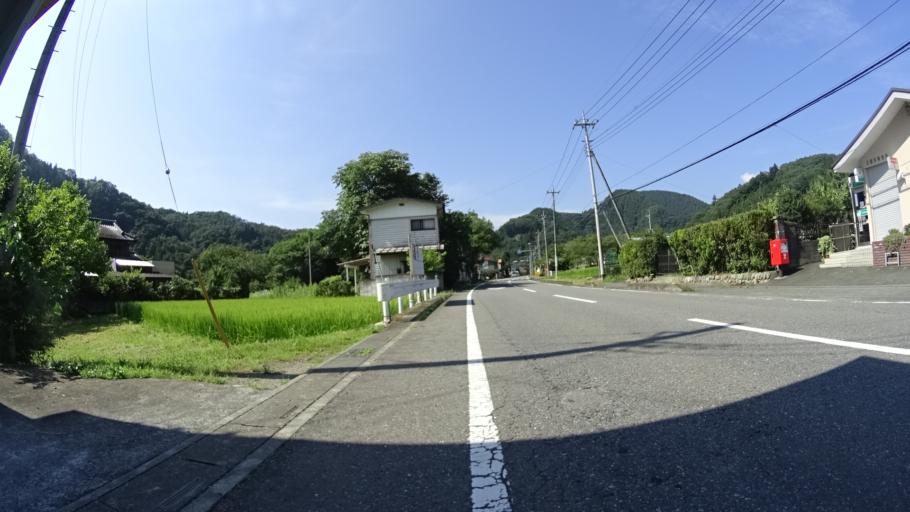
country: JP
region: Saitama
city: Chichibu
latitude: 36.0276
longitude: 138.9709
